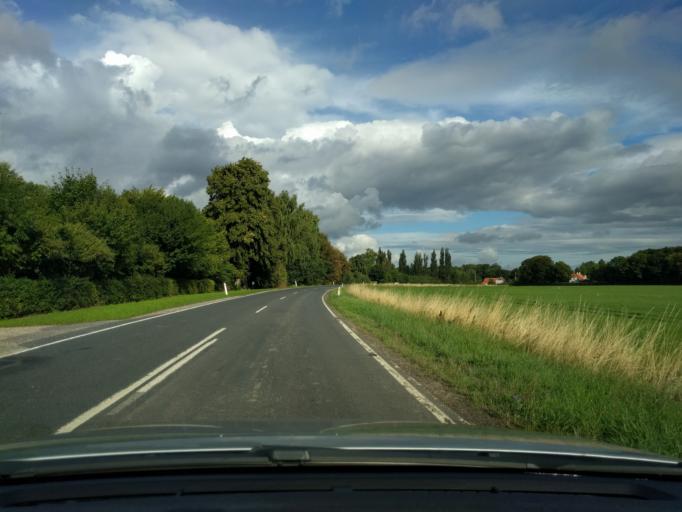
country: DK
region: South Denmark
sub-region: Kerteminde Kommune
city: Kerteminde
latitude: 55.4061
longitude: 10.6630
